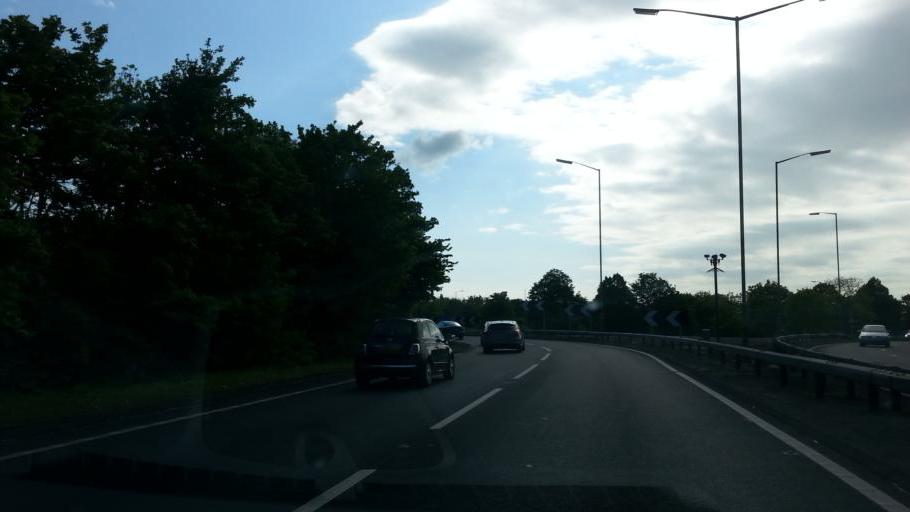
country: GB
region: England
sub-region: Peterborough
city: Peterborough
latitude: 52.5650
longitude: -0.2828
